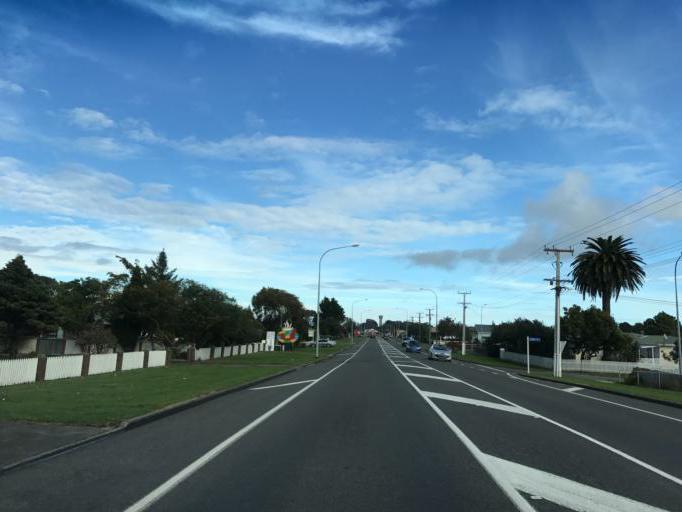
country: NZ
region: Manawatu-Wanganui
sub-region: Horowhenua District
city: Foxton
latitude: -40.4670
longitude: 175.2879
